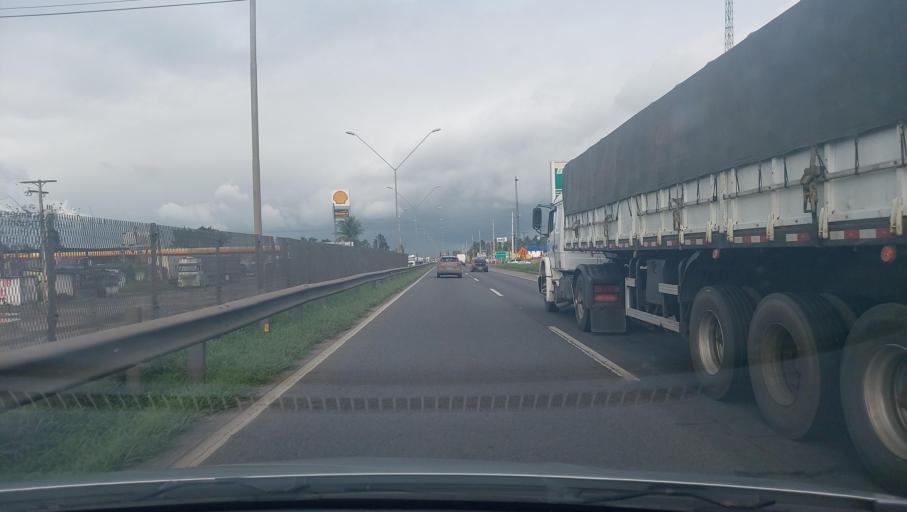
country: BR
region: Bahia
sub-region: Feira De Santana
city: Feira de Santana
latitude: -12.3146
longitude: -38.8800
